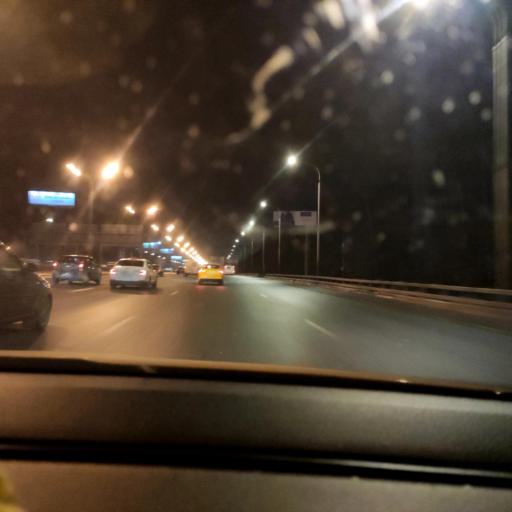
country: RU
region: Moscow
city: Babushkin
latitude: 55.8773
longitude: 37.7343
